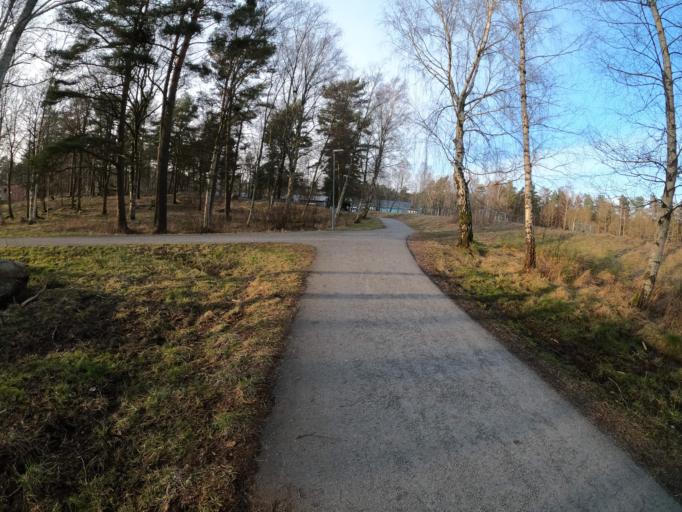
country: SE
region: Vaestra Goetaland
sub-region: Harryda Kommun
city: Molnlycke
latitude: 57.6498
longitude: 12.1208
